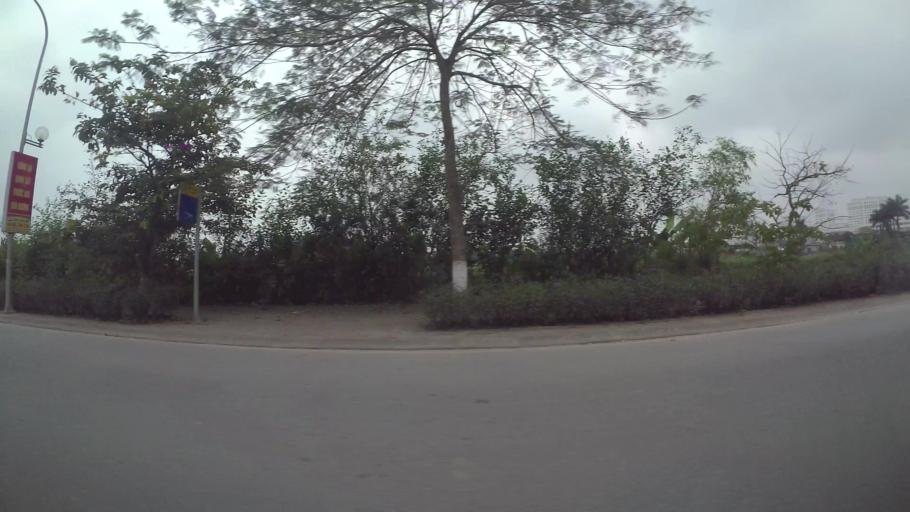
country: VN
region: Ha Noi
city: Trau Quy
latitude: 21.0542
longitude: 105.9195
